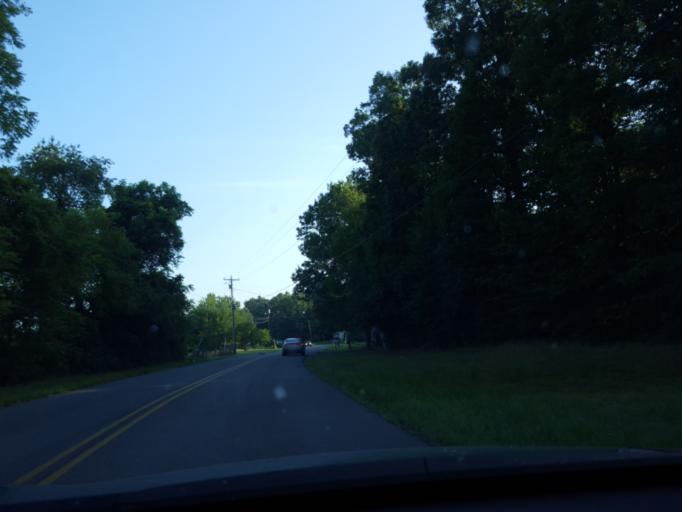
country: US
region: Virginia
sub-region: Augusta County
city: Lyndhurst
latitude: 38.0117
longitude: -78.9497
